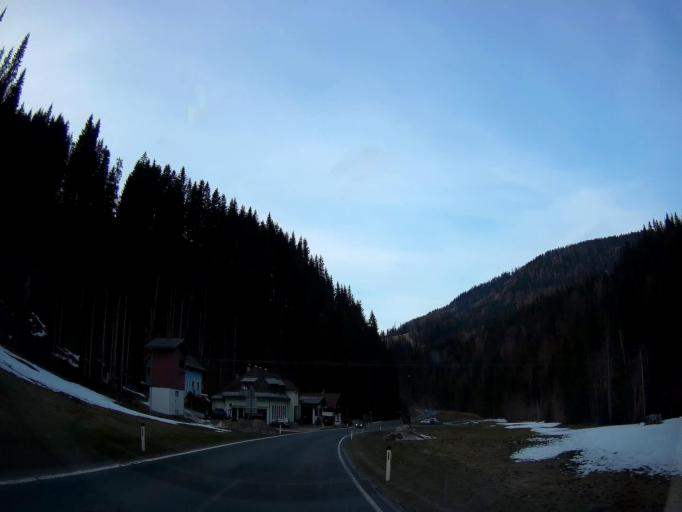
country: AT
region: Salzburg
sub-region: Politischer Bezirk Hallein
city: Abtenau
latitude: 47.5470
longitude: 13.4124
